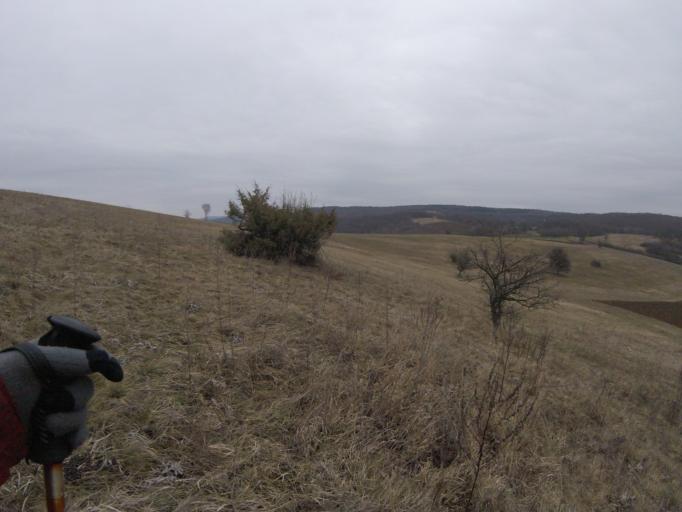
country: HU
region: Borsod-Abauj-Zemplen
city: Rudabanya
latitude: 48.4669
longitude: 20.6081
